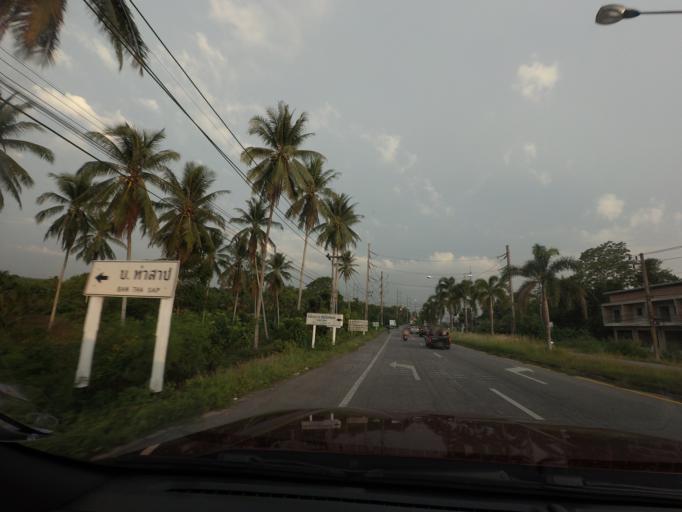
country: TH
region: Yala
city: Yala
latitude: 6.5758
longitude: 101.1992
